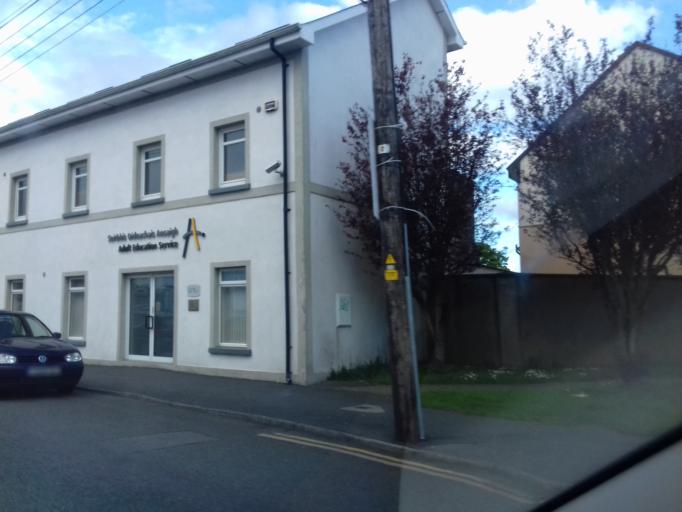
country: IE
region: Leinster
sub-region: Kilkenny
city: Kilkenny
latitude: 52.6450
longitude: -7.2498
